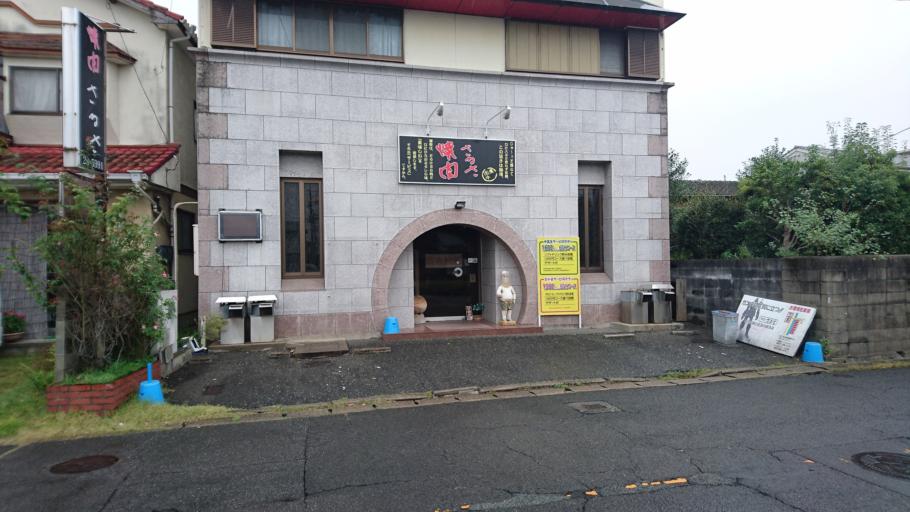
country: JP
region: Saga Prefecture
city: Saga-shi
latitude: 33.2447
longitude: 130.2945
